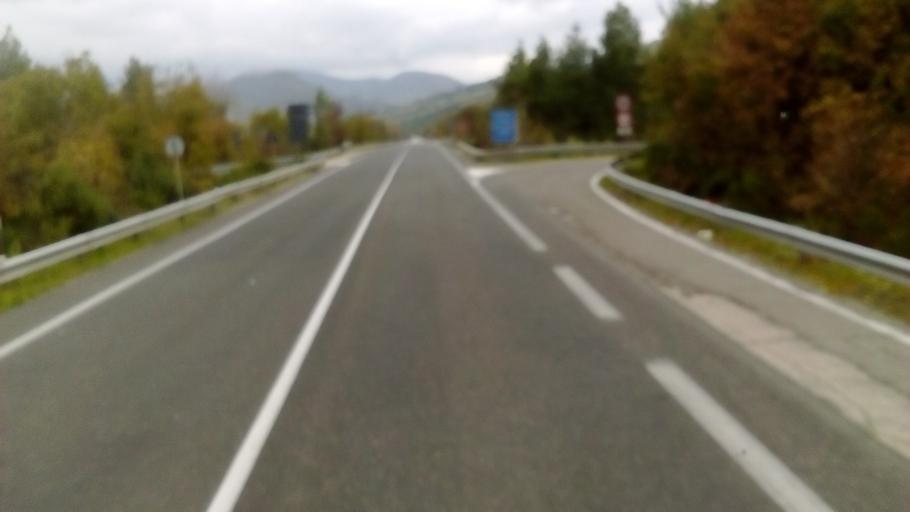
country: IT
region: Abruzzo
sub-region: Provincia di Chieti
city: San Giovanni Lipioni
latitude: 41.8277
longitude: 14.5740
